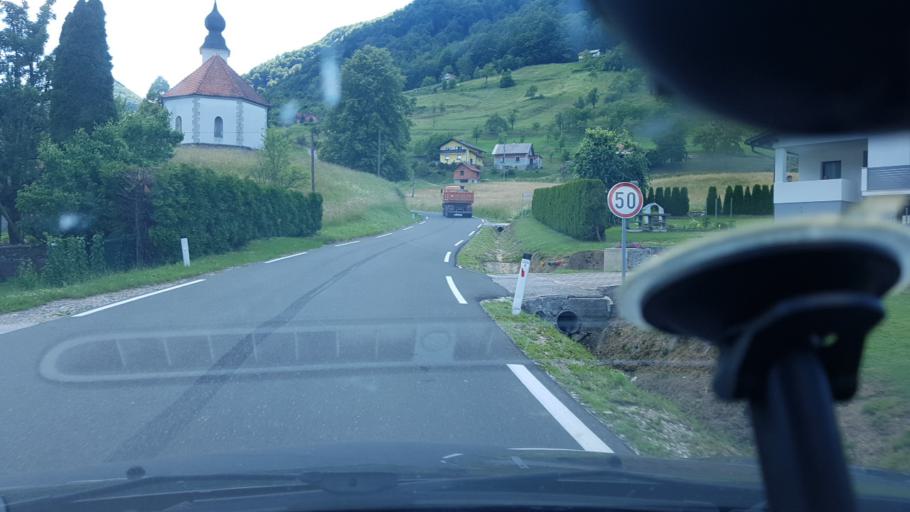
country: SI
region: Zetale
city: Zetale
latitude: 46.2696
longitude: 15.7810
